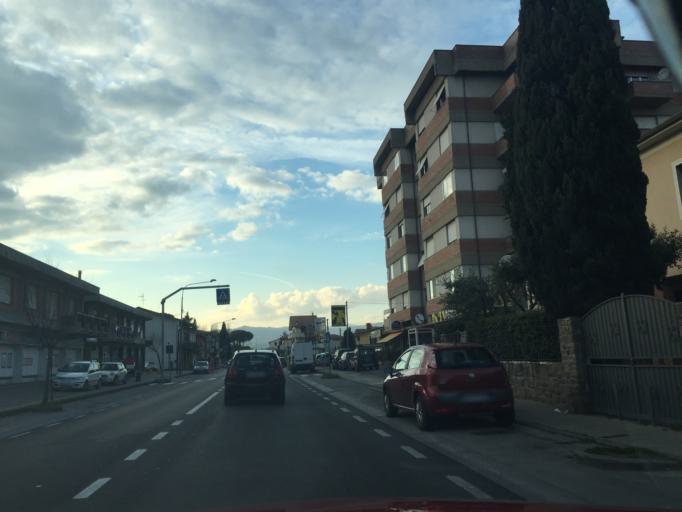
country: IT
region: Tuscany
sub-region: Provincia di Pistoia
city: Monsummano Terme
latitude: 43.8731
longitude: 10.8062
